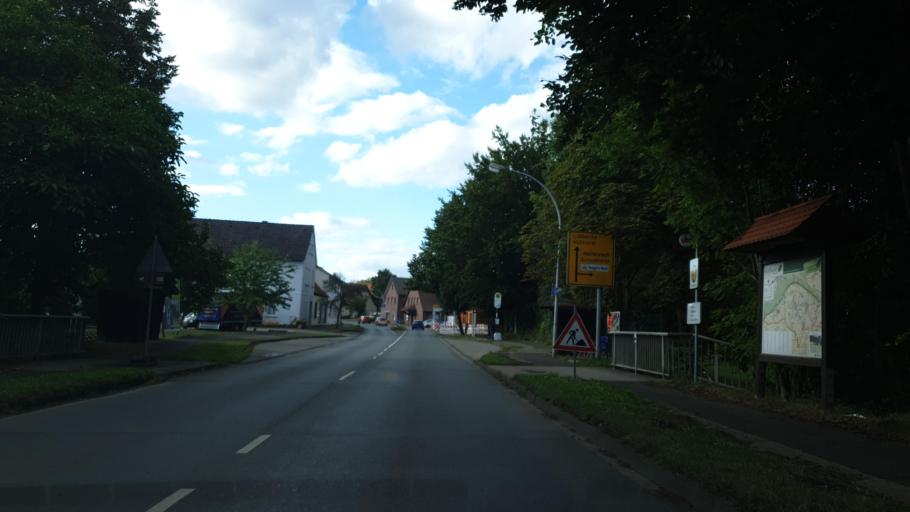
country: DE
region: North Rhine-Westphalia
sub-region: Regierungsbezirk Detmold
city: Huellhorst
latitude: 52.2532
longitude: 8.6991
